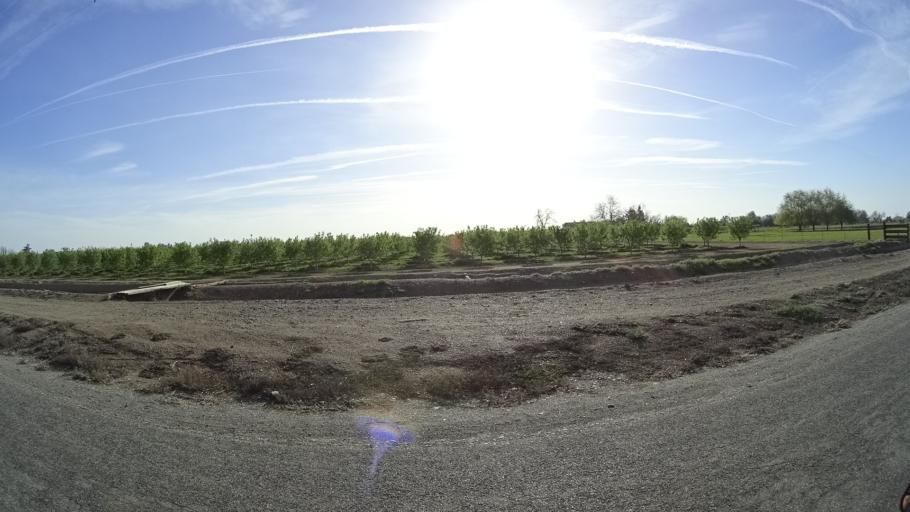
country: US
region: California
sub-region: Glenn County
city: Orland
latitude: 39.7213
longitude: -122.2348
